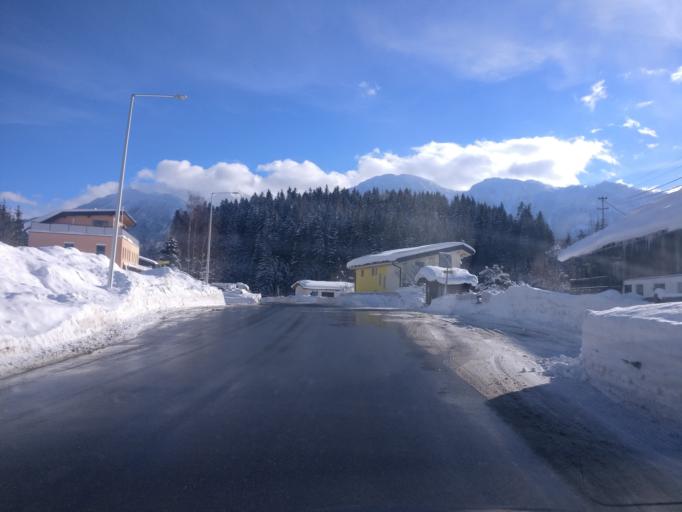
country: AT
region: Salzburg
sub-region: Politischer Bezirk Sankt Johann im Pongau
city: Goldegg
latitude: 47.3235
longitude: 13.0849
